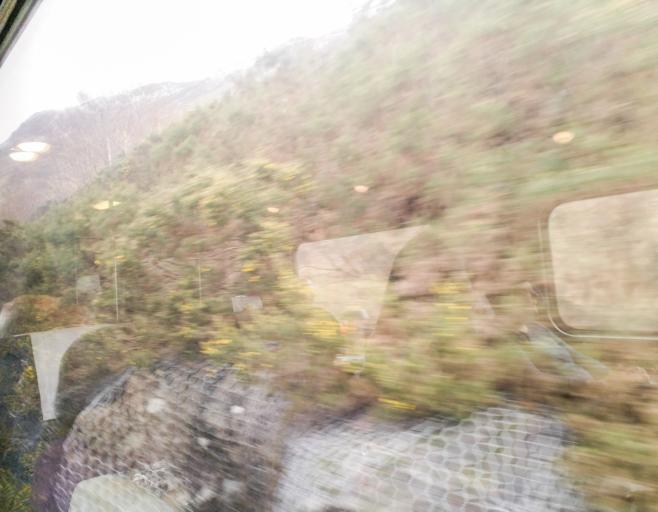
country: GB
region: Scotland
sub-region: Highland
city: Spean Bridge
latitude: 56.8217
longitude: -4.7129
